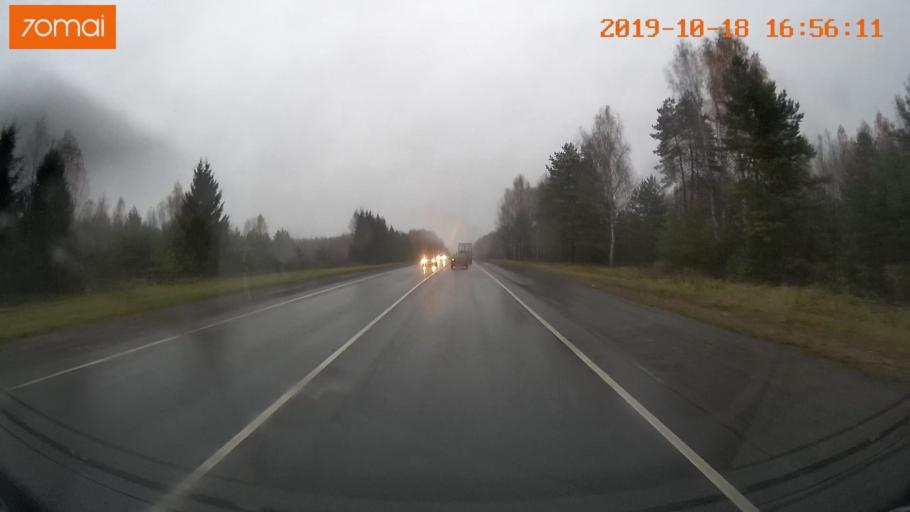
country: RU
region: Ivanovo
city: Novoye Leushino
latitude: 56.6541
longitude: 40.5862
